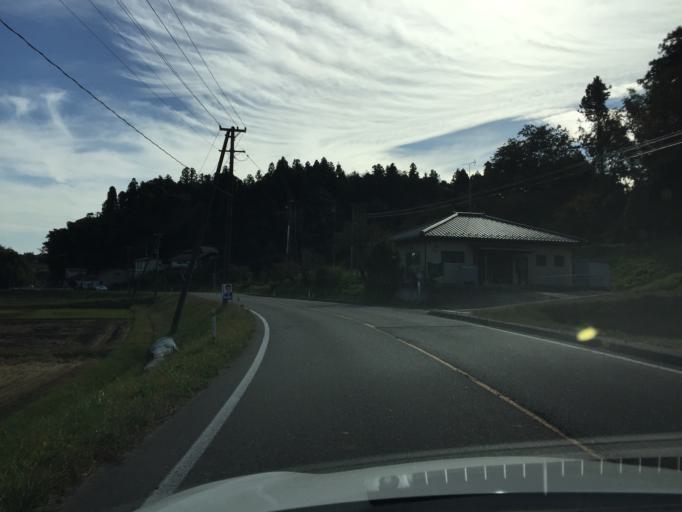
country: JP
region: Fukushima
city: Miharu
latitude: 37.4069
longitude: 140.4570
